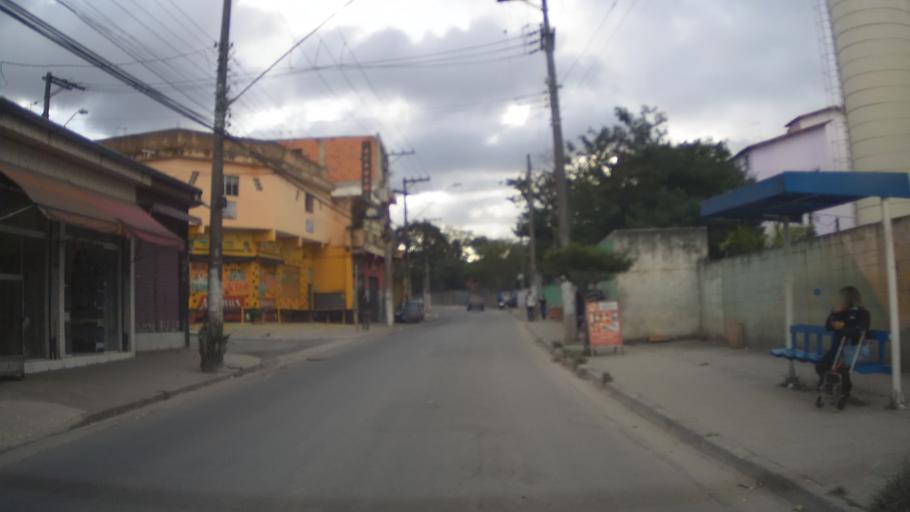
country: BR
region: Sao Paulo
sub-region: Itaquaquecetuba
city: Itaquaquecetuba
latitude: -23.4634
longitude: -46.3954
